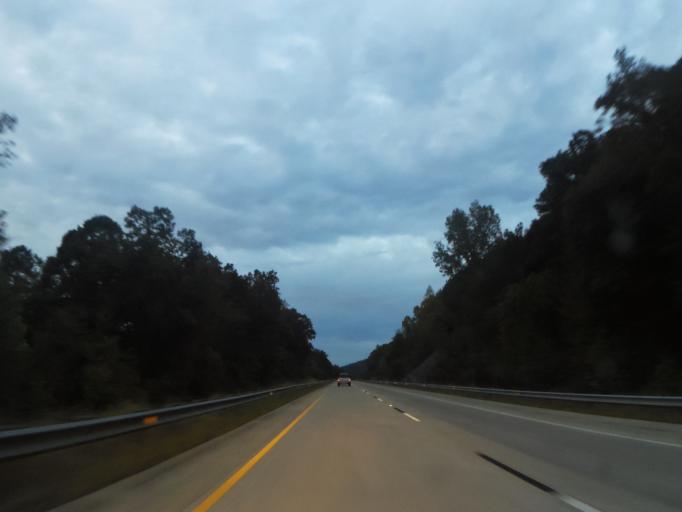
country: US
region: Alabama
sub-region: Etowah County
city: Whitesboro
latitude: 34.1109
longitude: -85.9909
